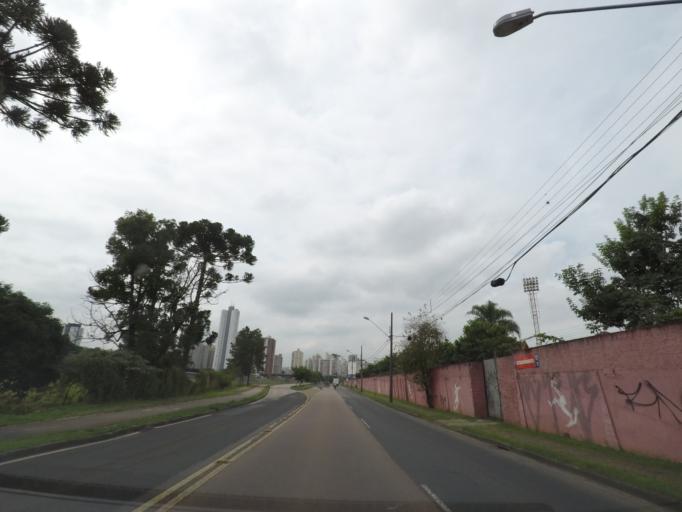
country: BR
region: Parana
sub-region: Curitiba
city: Curitiba
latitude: -25.4393
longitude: -49.2577
